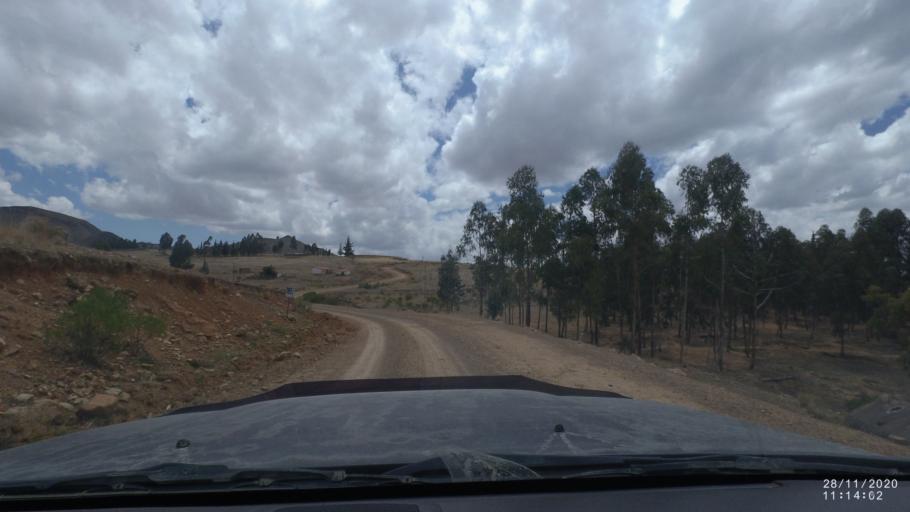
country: BO
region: Cochabamba
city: Tarata
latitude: -17.7463
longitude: -66.1003
